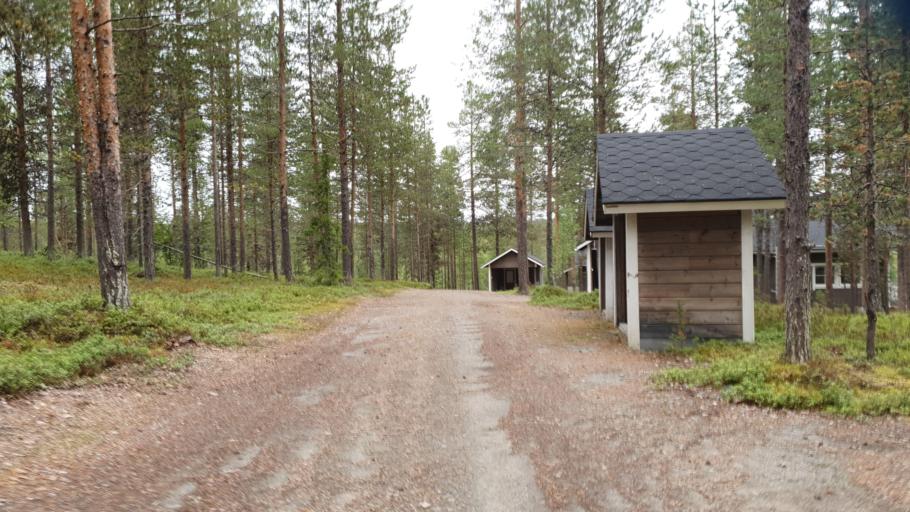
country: FI
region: Lapland
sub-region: Tunturi-Lappi
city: Kolari
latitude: 67.6016
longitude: 24.2010
